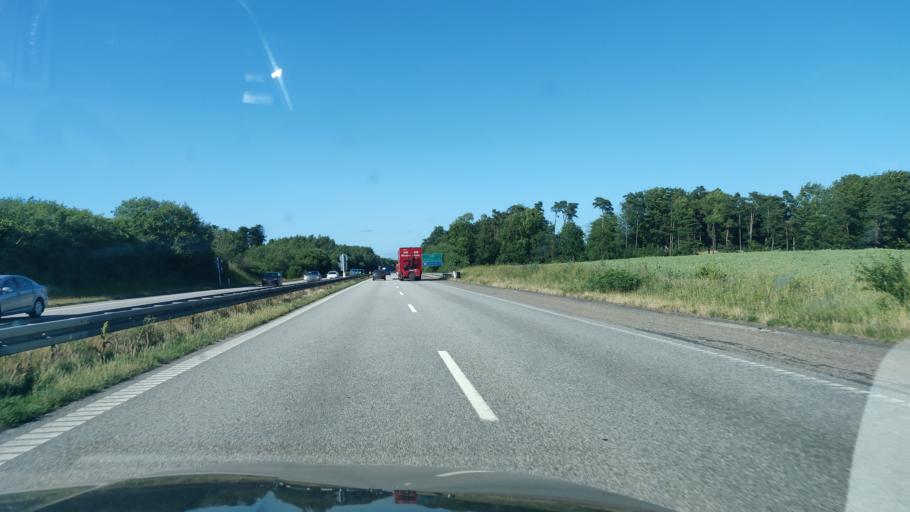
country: DK
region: North Denmark
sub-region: Rebild Kommune
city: Stovring
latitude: 56.9151
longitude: 9.8416
